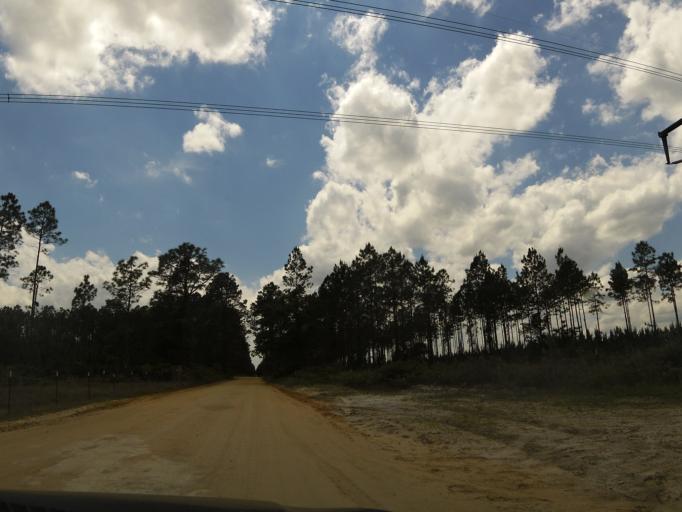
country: US
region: Florida
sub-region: Clay County
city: Asbury Lake
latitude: 29.8972
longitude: -81.8472
